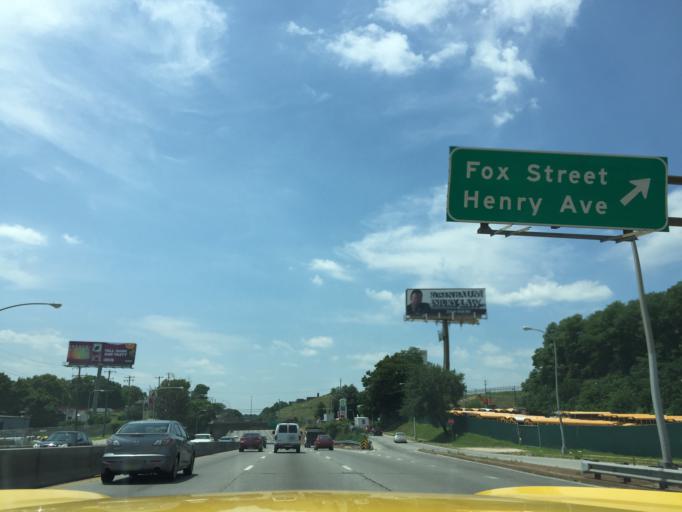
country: US
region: Pennsylvania
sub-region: Montgomery County
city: Bala-Cynwyd
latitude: 40.0160
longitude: -75.1760
